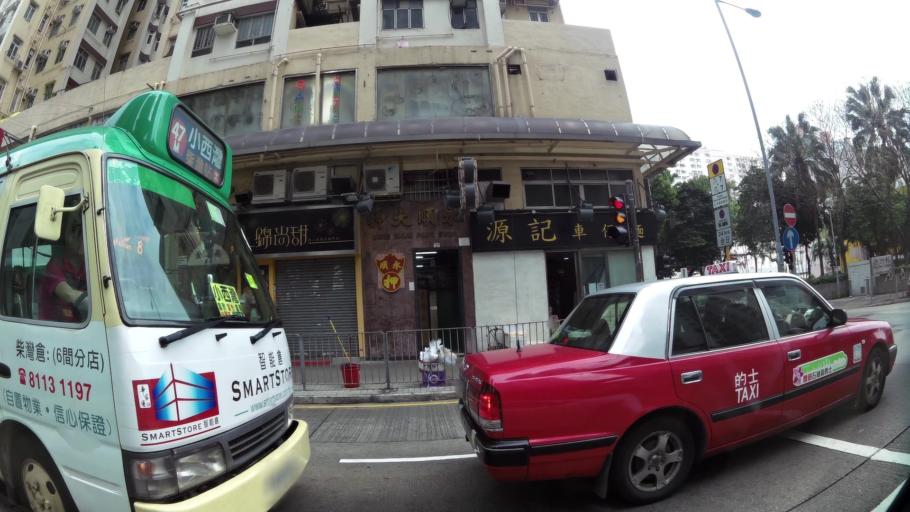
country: HK
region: Wanchai
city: Wan Chai
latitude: 22.2646
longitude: 114.2406
